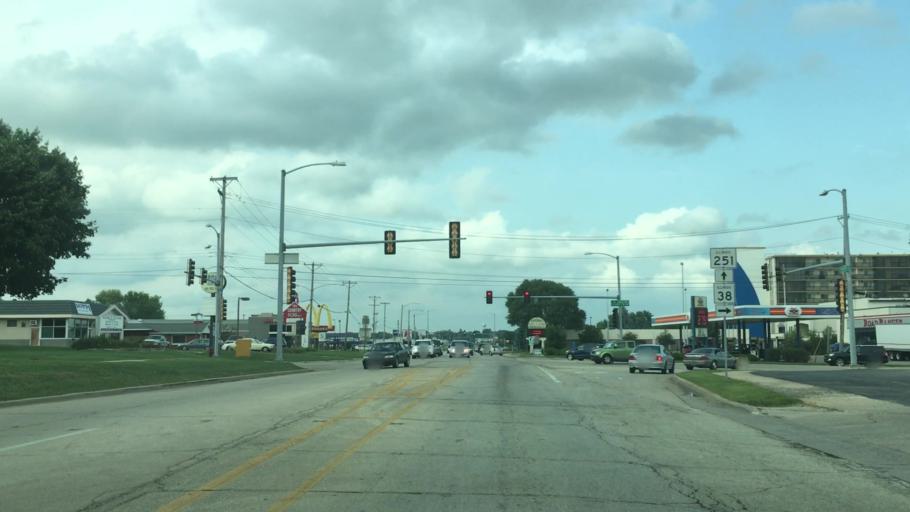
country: US
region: Illinois
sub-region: Ogle County
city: Rochelle
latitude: 41.9334
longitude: -89.0683
